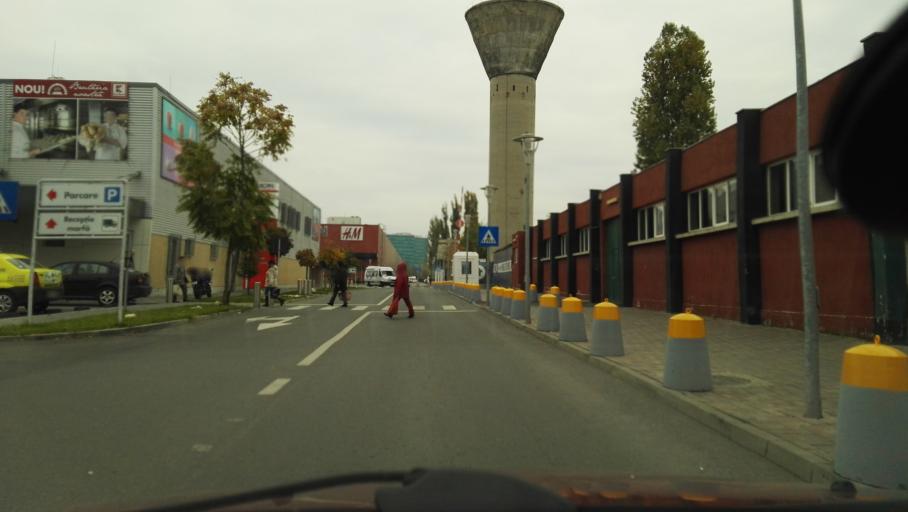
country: RO
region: Bucuresti
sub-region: Municipiul Bucuresti
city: Bucuresti
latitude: 44.4160
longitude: 26.0711
